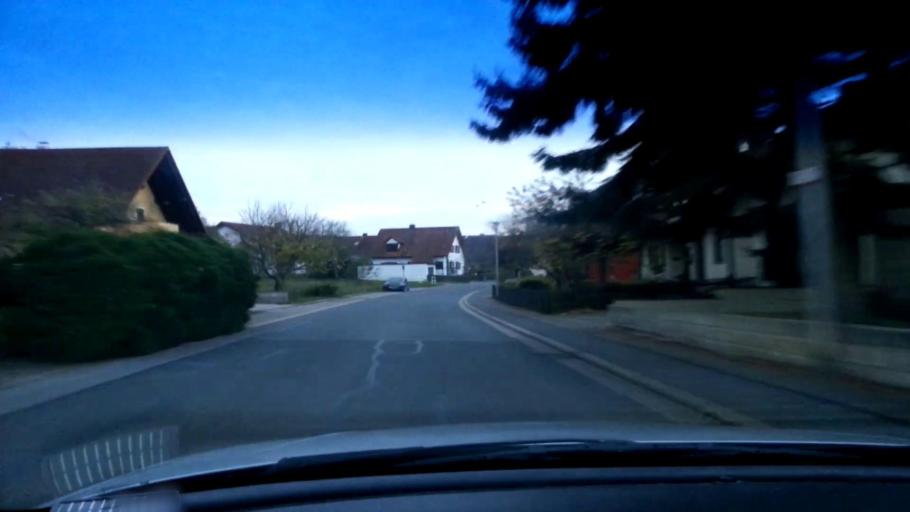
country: DE
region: Bavaria
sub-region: Upper Franconia
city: Breitengussbach
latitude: 49.9749
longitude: 10.8967
